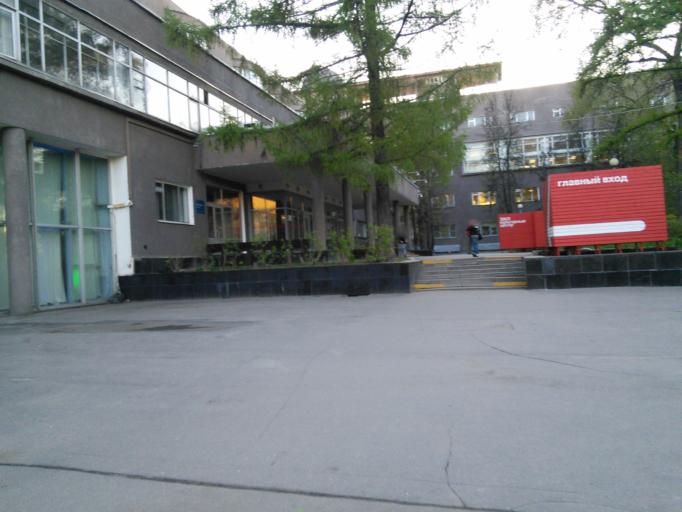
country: RU
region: Moskovskaya
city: Kozhukhovo
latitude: 55.7145
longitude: 37.6584
